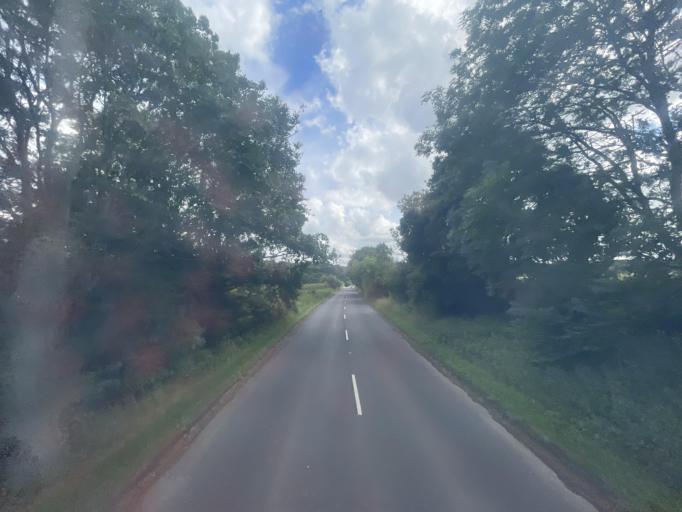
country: GB
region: England
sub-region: Kent
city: Westerham
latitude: 51.2744
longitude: 0.0855
